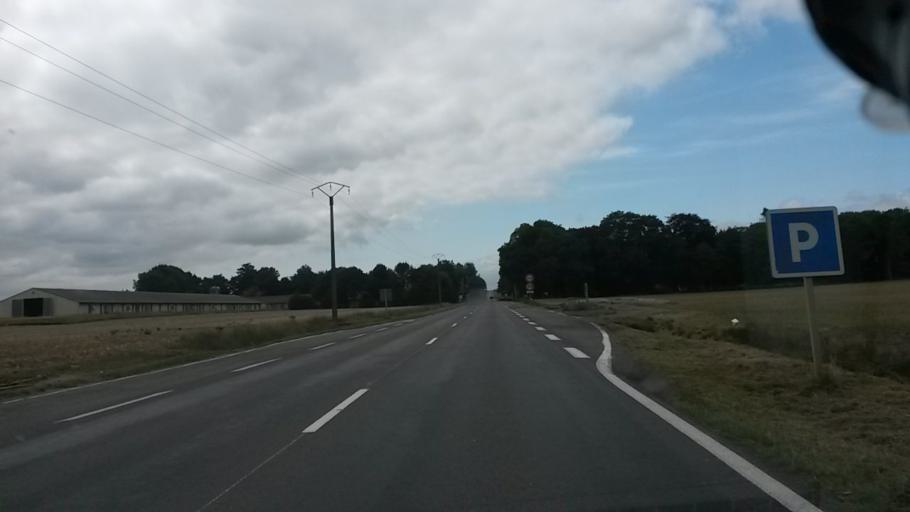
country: FR
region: Nord-Pas-de-Calais
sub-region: Departement du Pas-de-Calais
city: Bourlon
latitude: 50.1555
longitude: 3.1066
